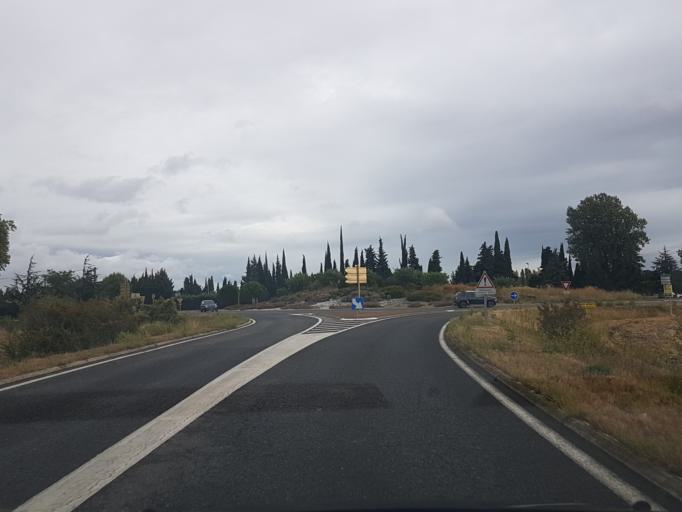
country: FR
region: Languedoc-Roussillon
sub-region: Departement de l'Aude
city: Bram
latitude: 43.2383
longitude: 2.1040
